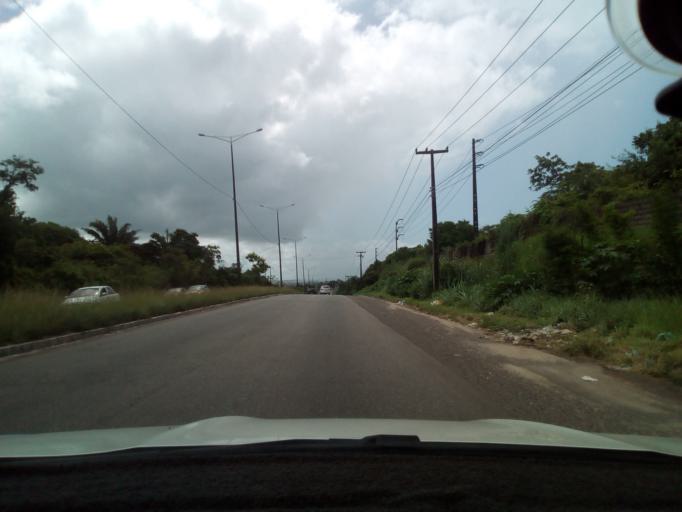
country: BR
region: Paraiba
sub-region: Bayeux
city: Bayeux
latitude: -7.1419
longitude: -34.9056
